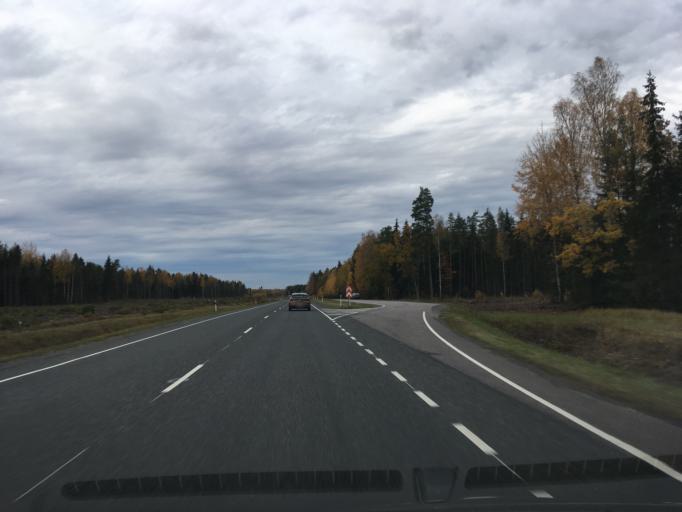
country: EE
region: Harju
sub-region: Nissi vald
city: Turba
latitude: 58.9595
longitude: 24.0748
